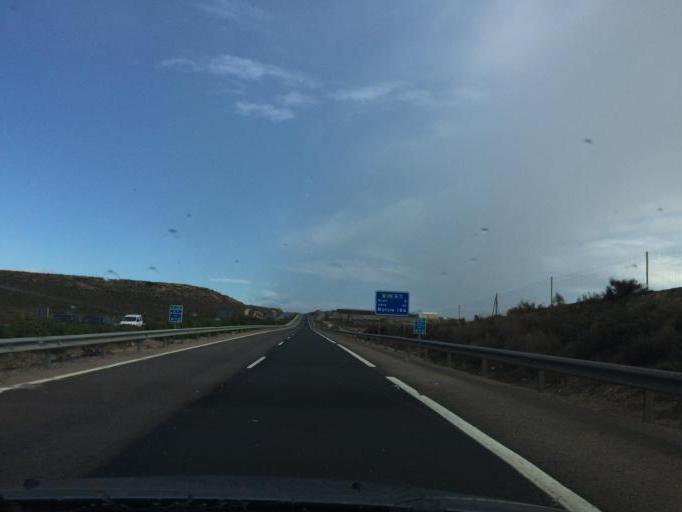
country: ES
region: Andalusia
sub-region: Provincia de Almeria
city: Nijar
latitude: 36.8749
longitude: -2.2239
